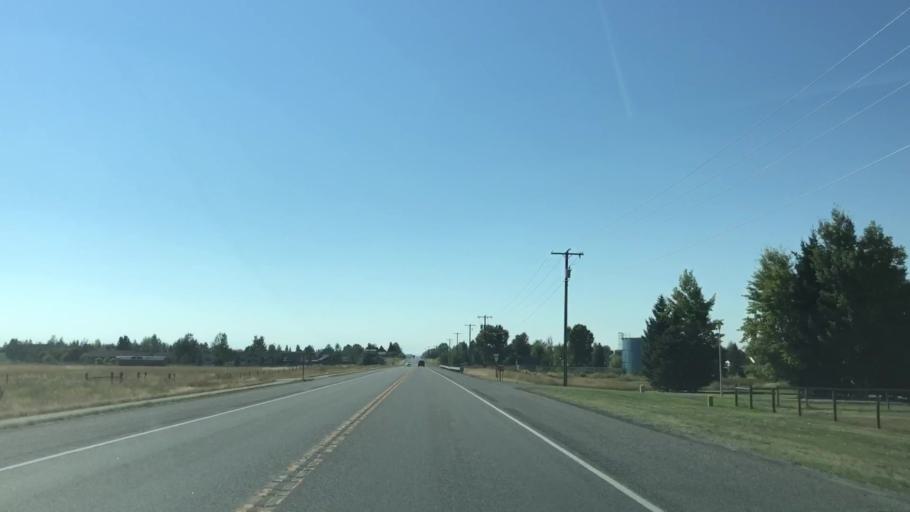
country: US
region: Montana
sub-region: Gallatin County
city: Belgrade
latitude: 45.7293
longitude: -111.1256
